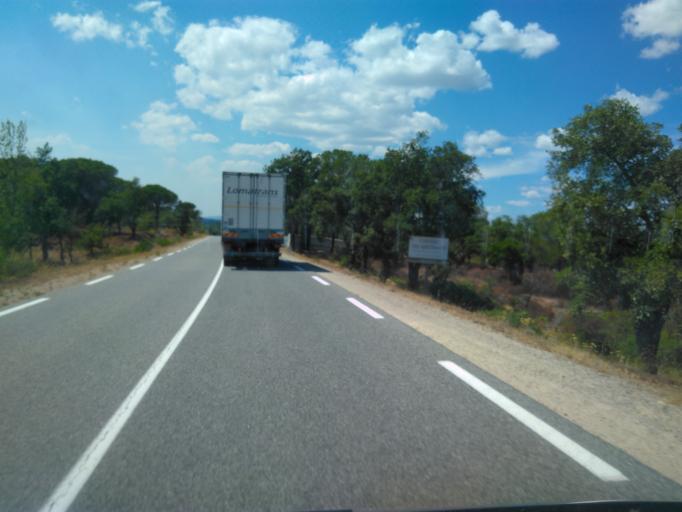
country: FR
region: Provence-Alpes-Cote d'Azur
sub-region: Departement du Var
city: Le Cannet-des-Maures
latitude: 43.3578
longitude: 6.4045
